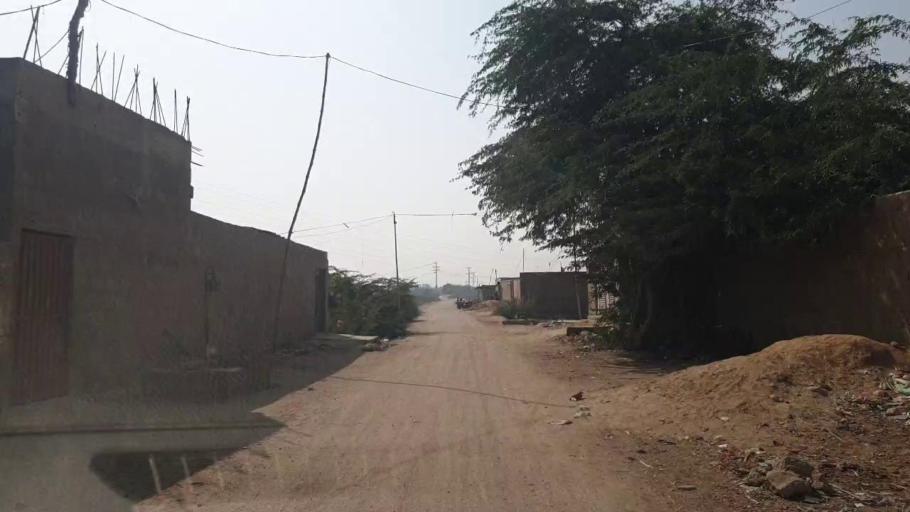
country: PK
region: Sindh
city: Kotri
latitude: 25.3427
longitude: 68.2842
